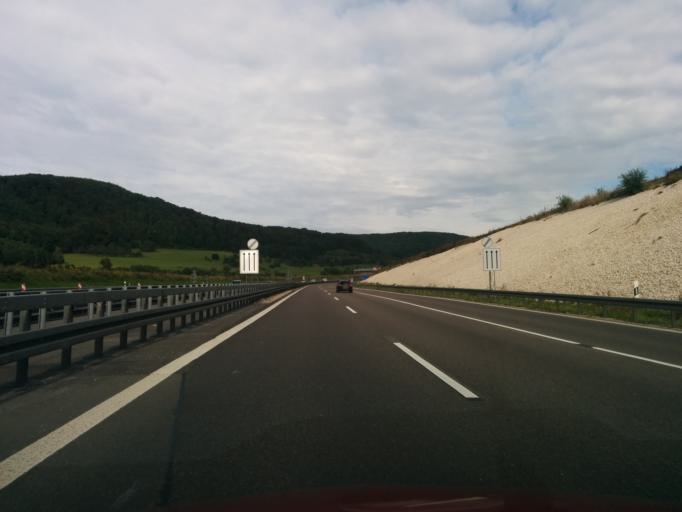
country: DE
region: Baden-Wuerttemberg
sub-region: Regierungsbezirk Stuttgart
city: Muhlhausen
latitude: 48.5850
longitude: 9.6596
